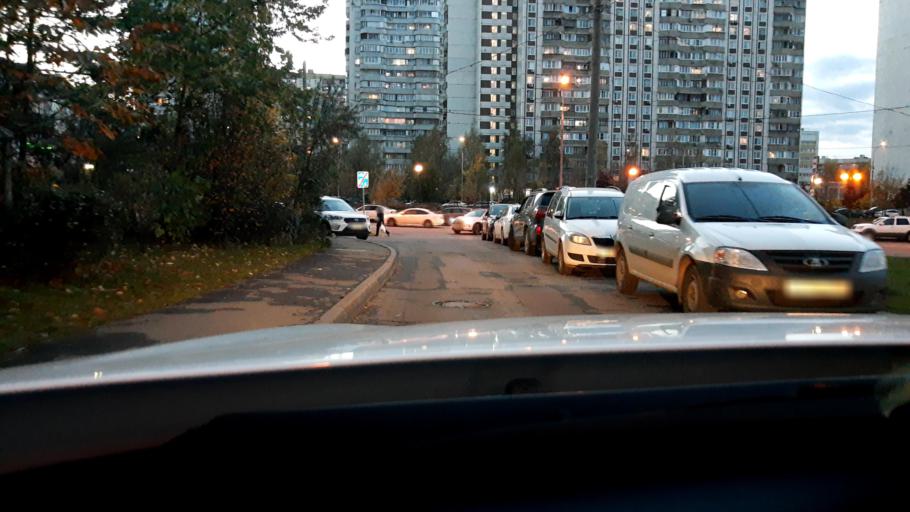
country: RU
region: Moskovskaya
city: Pavshino
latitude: 55.8539
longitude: 37.3544
